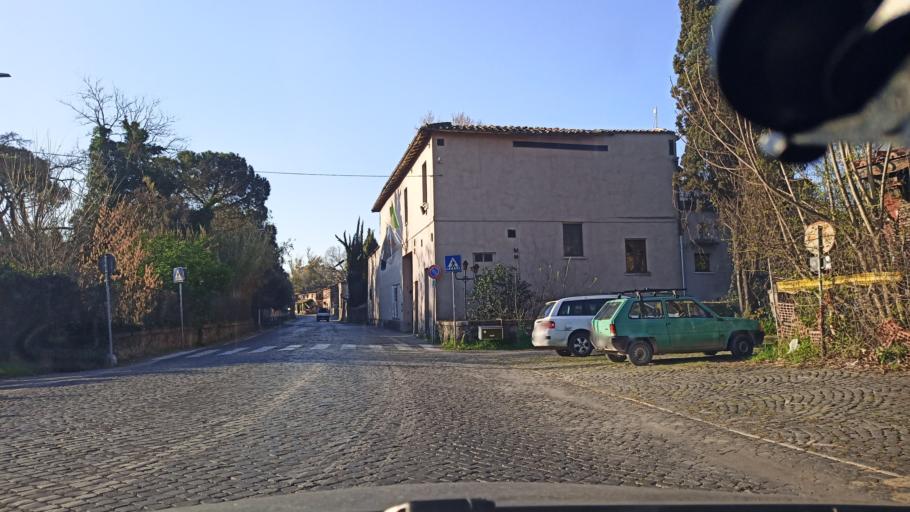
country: IT
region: Latium
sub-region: Citta metropolitana di Roma Capitale
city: Rome
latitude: 41.8687
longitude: 12.5023
